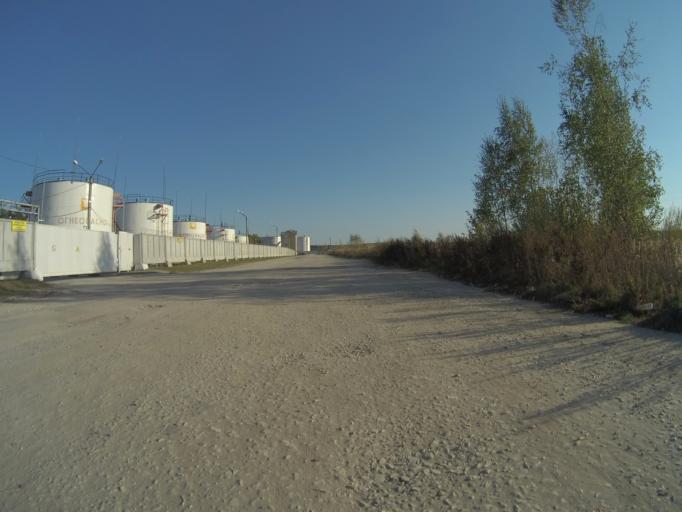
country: RU
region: Vladimir
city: Raduzhnyy
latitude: 56.0194
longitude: 40.3848
